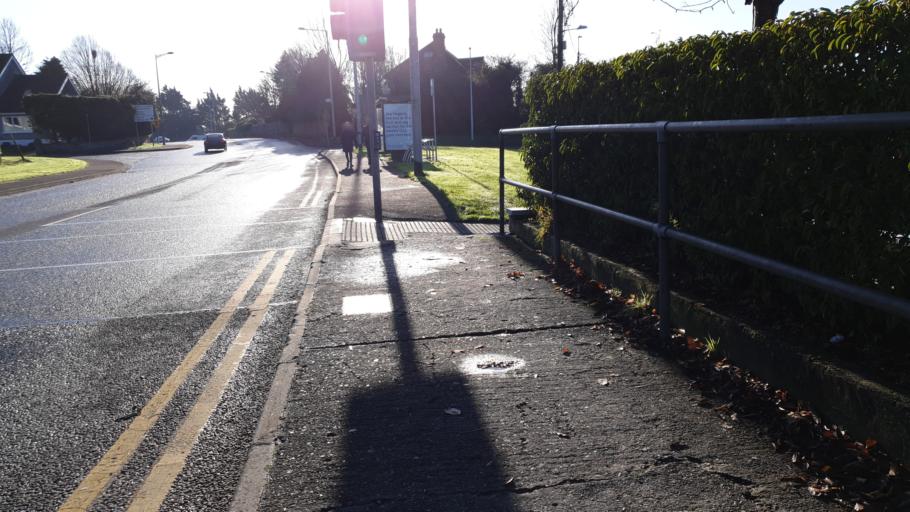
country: IE
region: Munster
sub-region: County Cork
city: Cork
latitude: 51.8876
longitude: -8.4330
